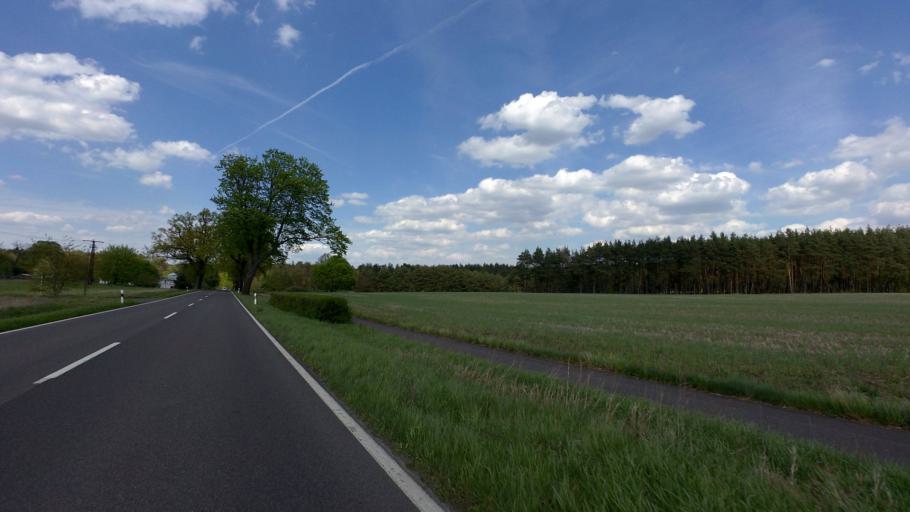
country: DE
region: Brandenburg
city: Milmersdorf
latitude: 53.0714
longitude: 13.6231
